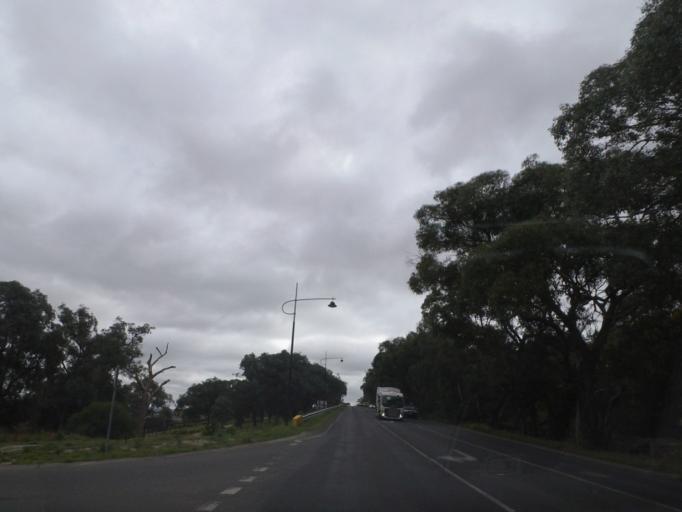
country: AU
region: Victoria
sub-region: Nillumbik
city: Doreen
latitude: -37.6197
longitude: 145.1358
